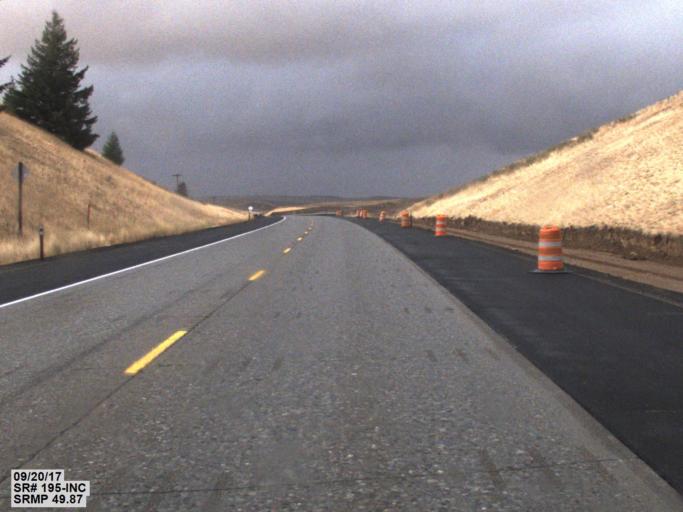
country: US
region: Washington
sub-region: Whitman County
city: Colfax
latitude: 47.0321
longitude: -117.3638
